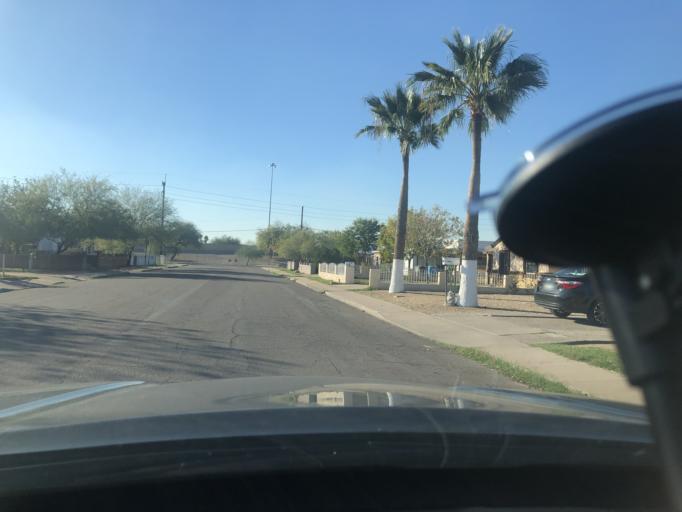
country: US
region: Arizona
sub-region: Maricopa County
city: Phoenix
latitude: 33.4577
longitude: -112.0346
